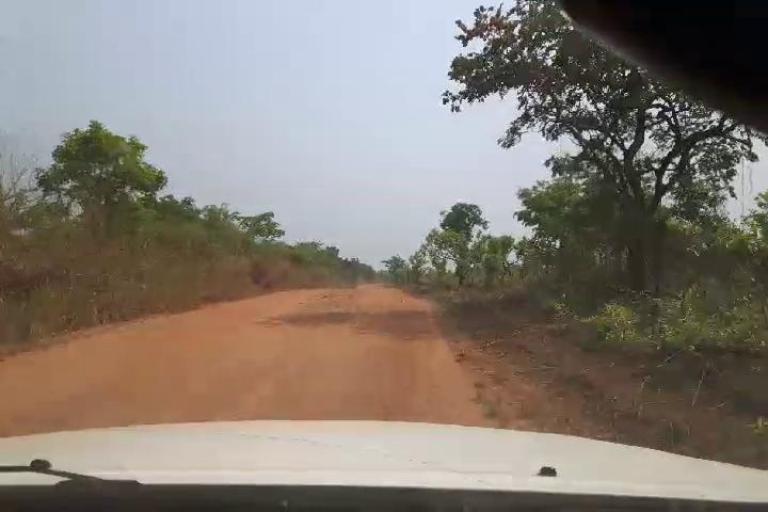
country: SL
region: Northern Province
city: Bumbuna
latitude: 8.9369
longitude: -11.8170
